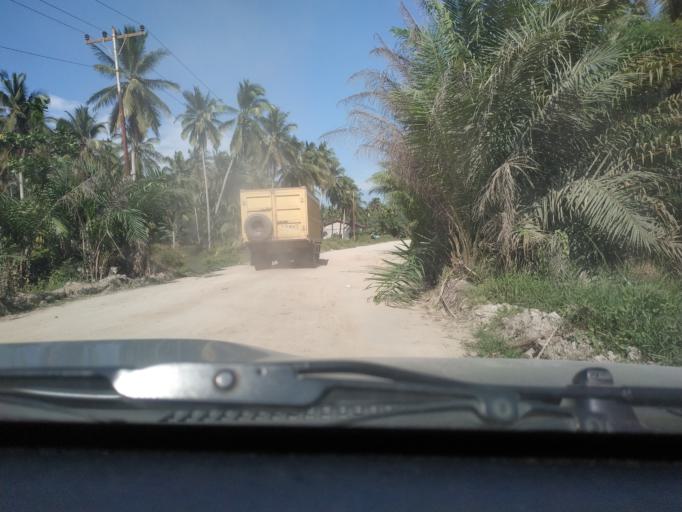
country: ID
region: North Sumatra
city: Tanjungbalai
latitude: 2.8375
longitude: 99.9669
